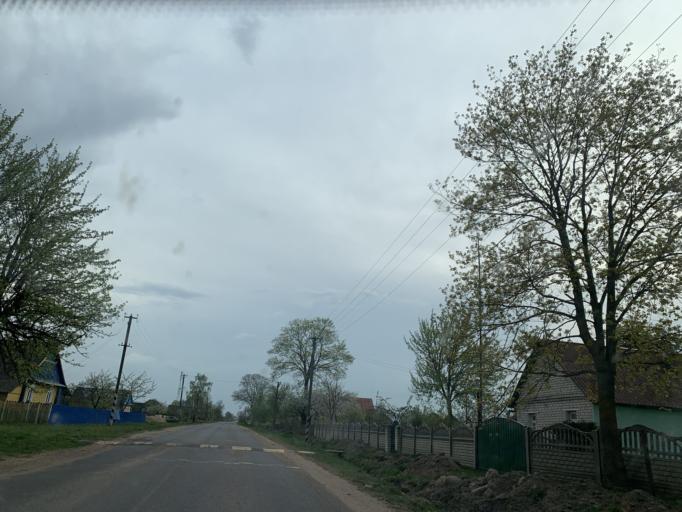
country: BY
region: Minsk
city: Kapyl'
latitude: 53.2836
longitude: 26.9817
